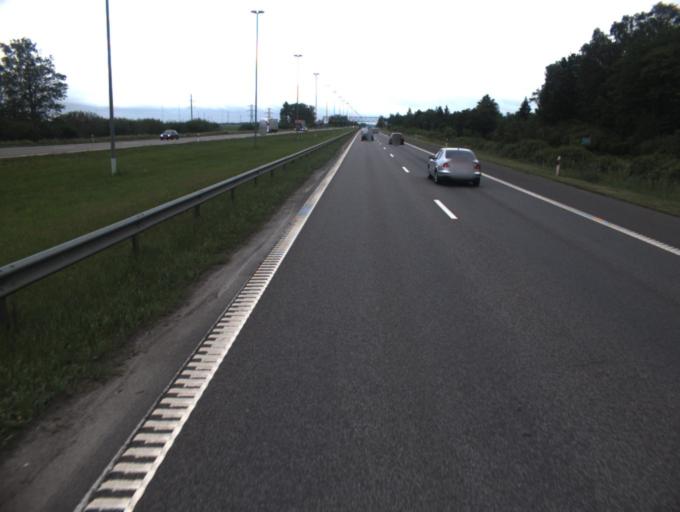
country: LT
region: Kauno apskritis
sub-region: Kaunas
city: Sargenai
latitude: 55.0062
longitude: 23.8393
